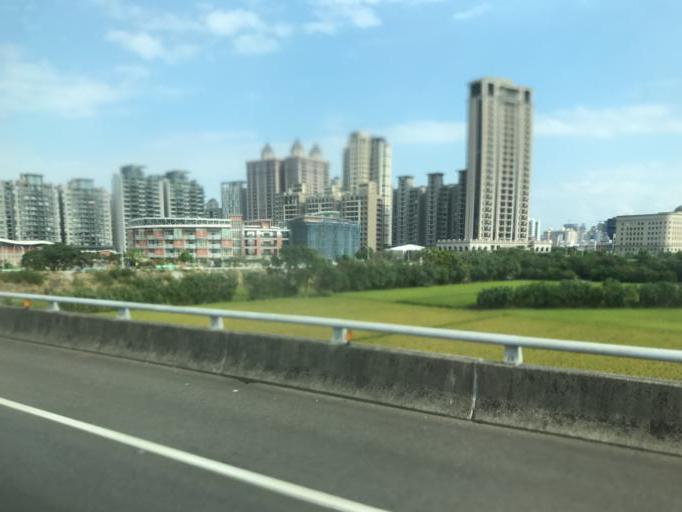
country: TW
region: Taiwan
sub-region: Hsinchu
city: Zhubei
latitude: 24.8147
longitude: 121.0124
